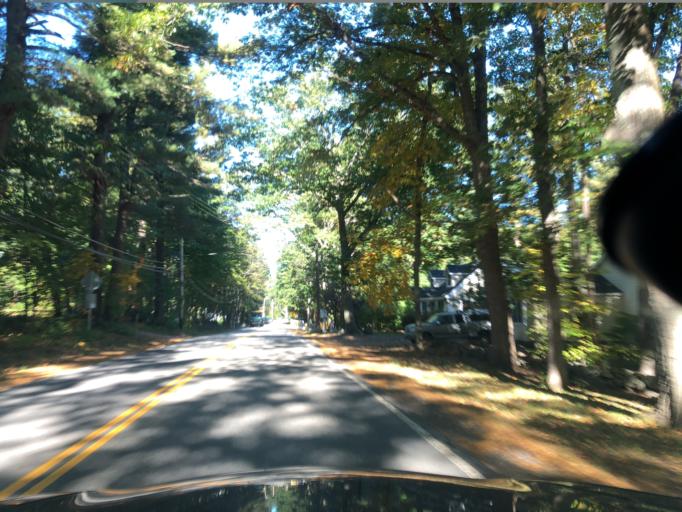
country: US
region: New Hampshire
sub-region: Rockingham County
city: Exeter
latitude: 43.0204
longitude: -70.9407
